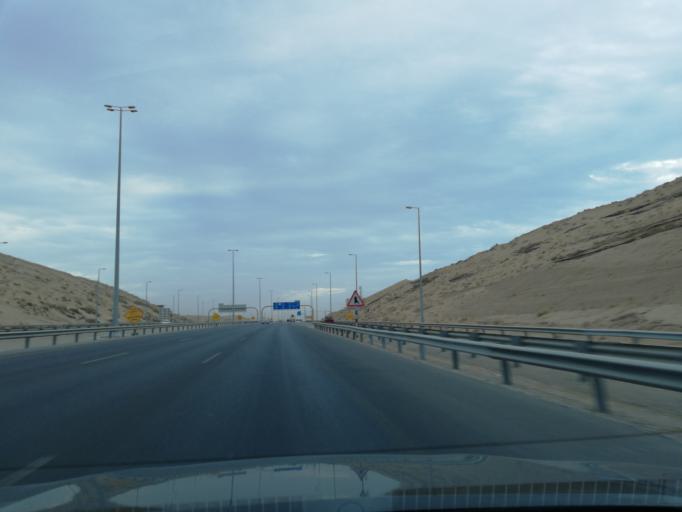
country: OM
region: Muhafazat Masqat
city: Bawshar
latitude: 23.5711
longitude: 58.4190
